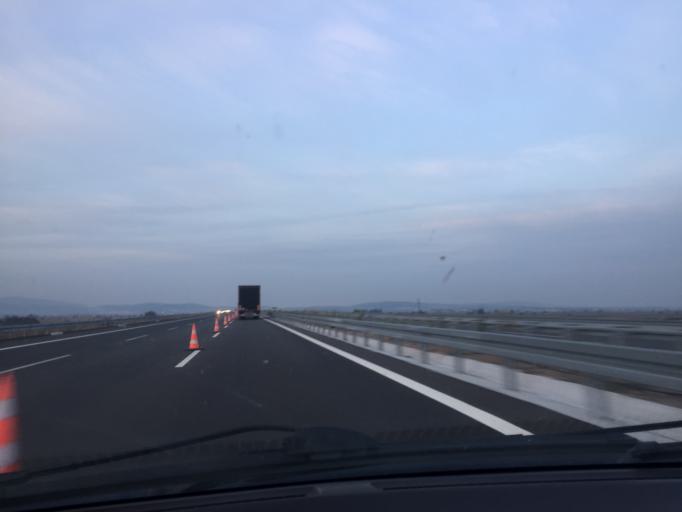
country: TR
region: Manisa
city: Halitpasa
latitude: 38.7311
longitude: 27.6556
